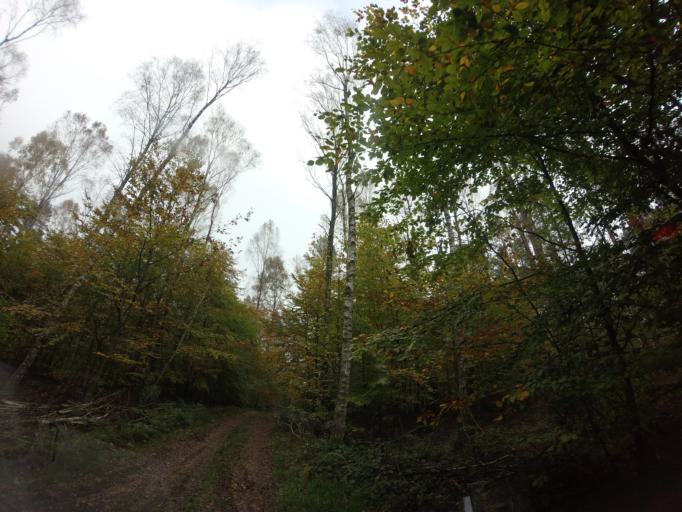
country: PL
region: West Pomeranian Voivodeship
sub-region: Powiat choszczenski
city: Bierzwnik
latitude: 53.1402
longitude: 15.6163
